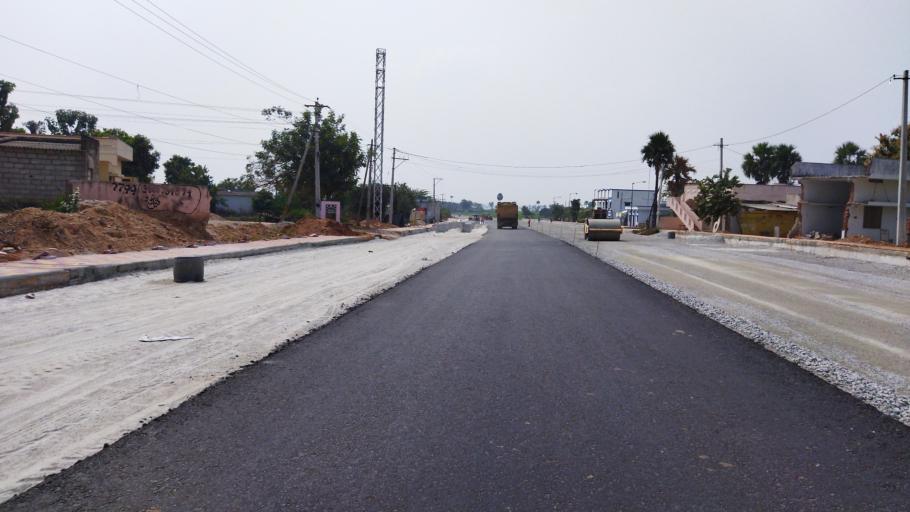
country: IN
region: Telangana
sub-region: Nalgonda
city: Nalgonda
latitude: 17.0900
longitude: 79.3287
